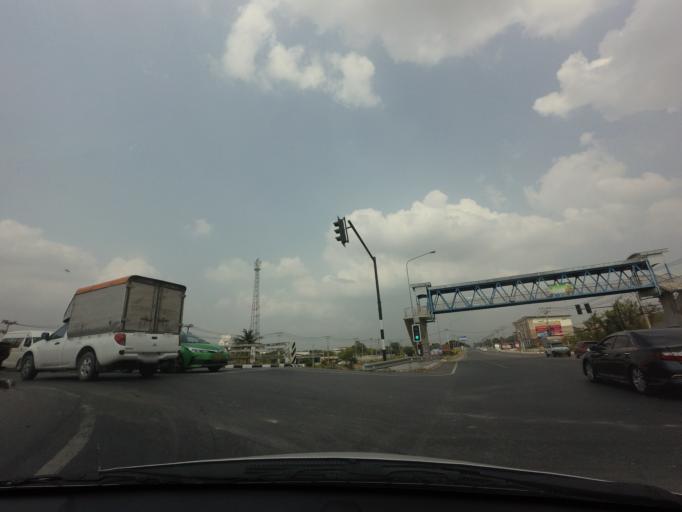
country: TH
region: Pathum Thani
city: Thanyaburi
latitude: 14.0670
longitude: 100.7102
